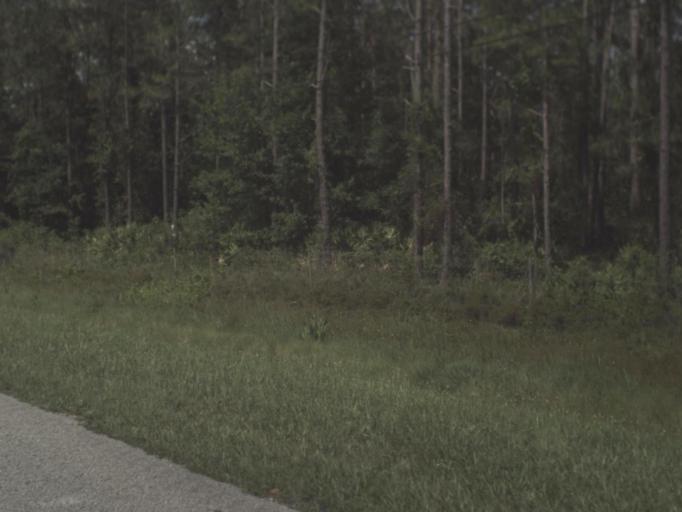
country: US
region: Florida
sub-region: Marion County
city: Citra
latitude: 29.4817
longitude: -82.1030
